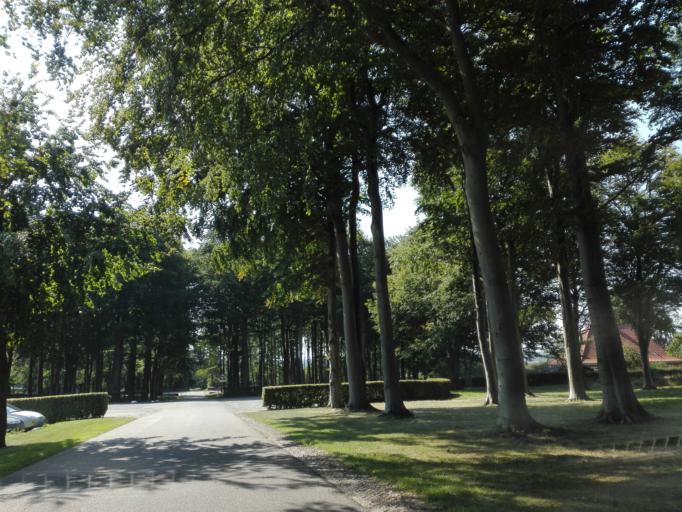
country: DK
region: Central Jutland
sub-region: Hedensted Kommune
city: Juelsminde
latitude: 55.7502
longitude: 10.0205
